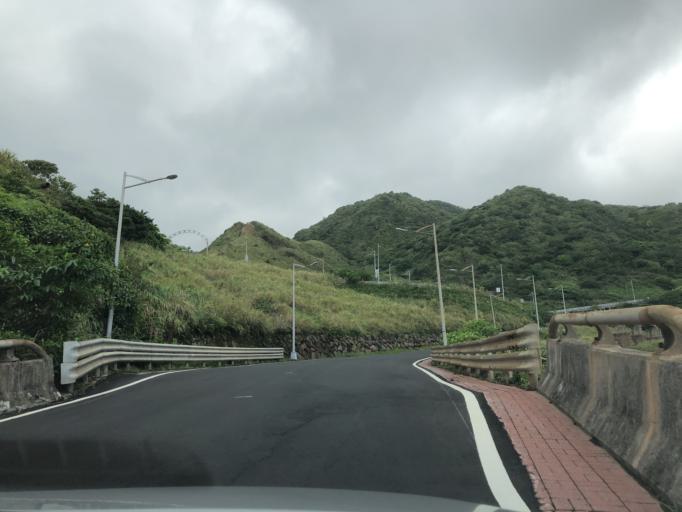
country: TW
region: Taiwan
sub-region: Keelung
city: Keelung
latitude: 25.1191
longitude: 121.8620
